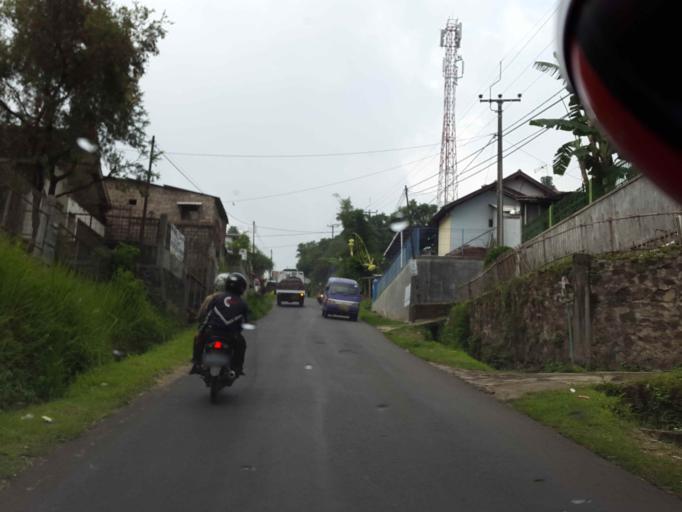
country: ID
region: West Java
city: Cimahi
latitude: -6.8354
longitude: 107.5742
